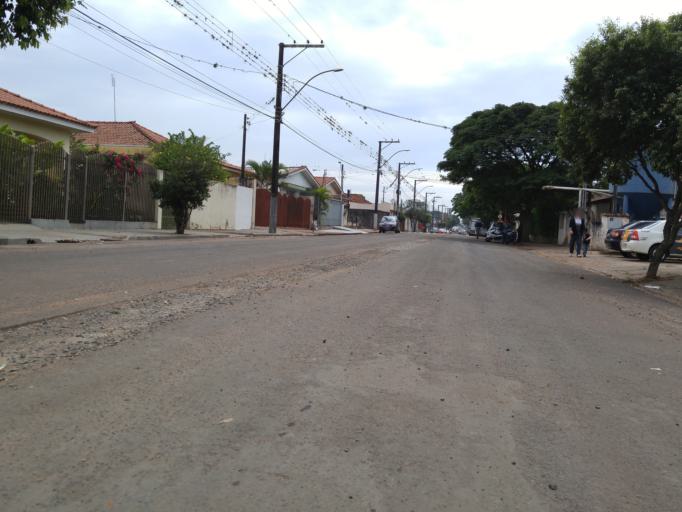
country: BR
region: Sao Paulo
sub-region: Paraguacu Paulista
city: Paraguacu Paulista
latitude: -22.4206
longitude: -50.5750
